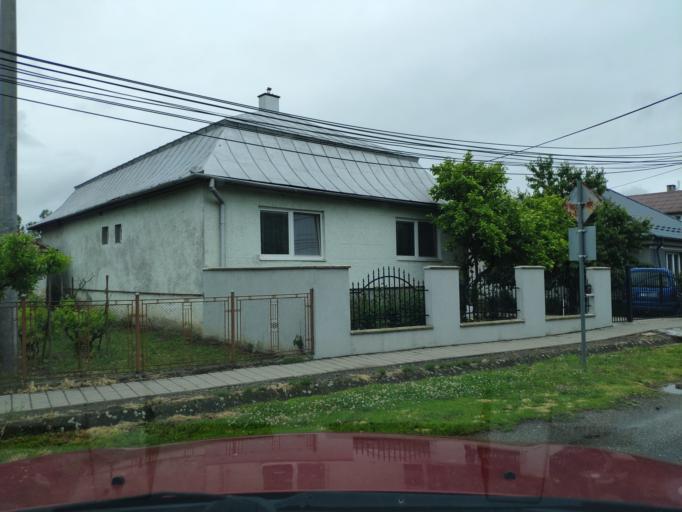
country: HU
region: Borsod-Abauj-Zemplen
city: Karcsa
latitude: 48.4030
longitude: 21.8094
